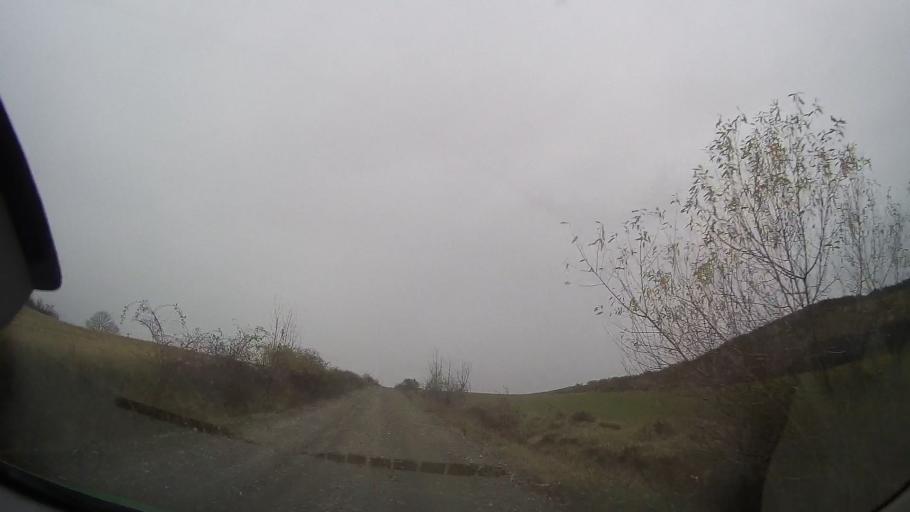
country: RO
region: Mures
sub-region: Comuna Ceausu de Campie
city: Ceausu de Campie
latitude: 46.6557
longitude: 24.4905
